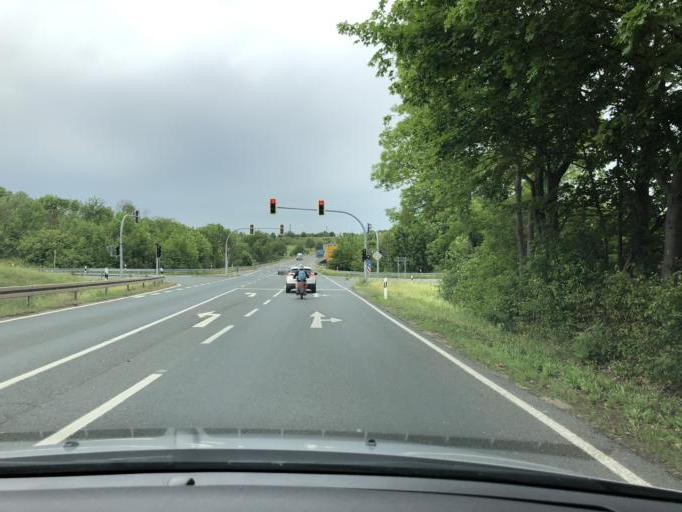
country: DE
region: Saxony-Anhalt
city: Burgwerben
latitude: 51.2172
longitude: 12.0014
